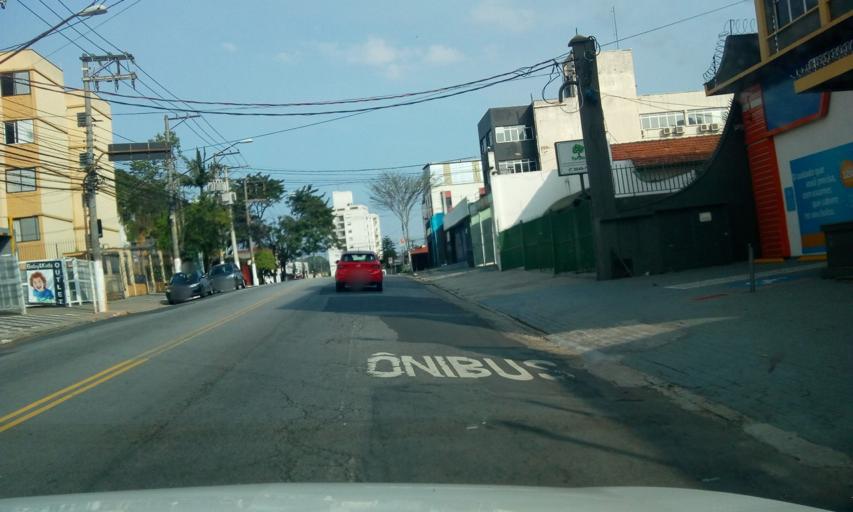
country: BR
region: Sao Paulo
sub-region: Osasco
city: Osasco
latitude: -23.5343
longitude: -46.7278
